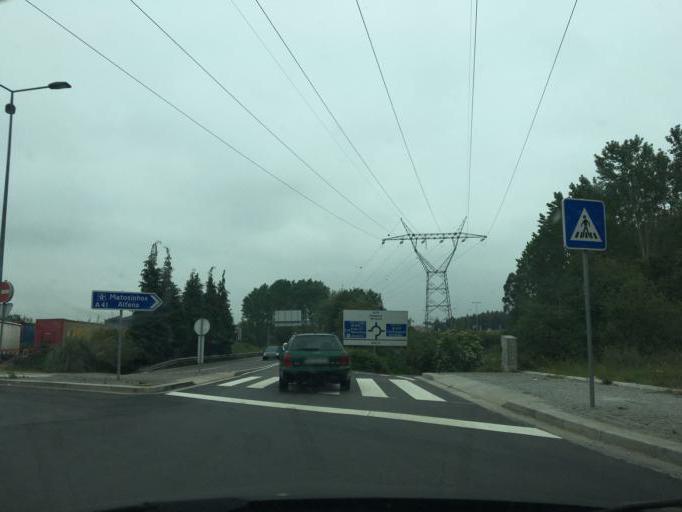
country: PT
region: Porto
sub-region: Maia
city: Nogueira
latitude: 41.2372
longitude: -8.5991
